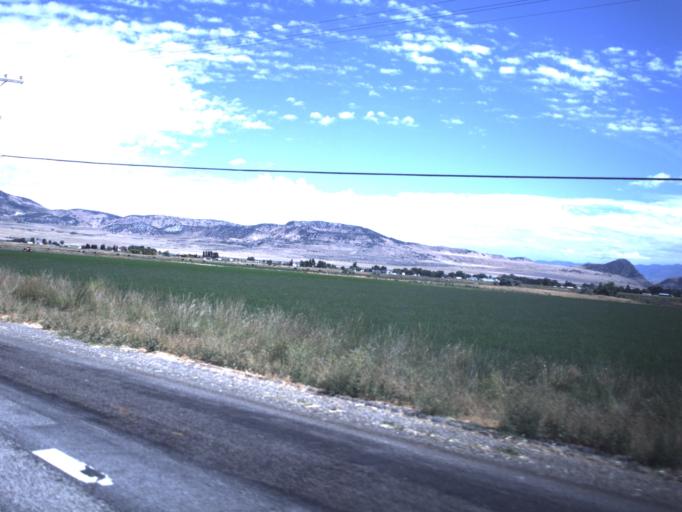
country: US
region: Utah
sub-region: Box Elder County
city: Garland
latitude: 41.8008
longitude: -112.1449
